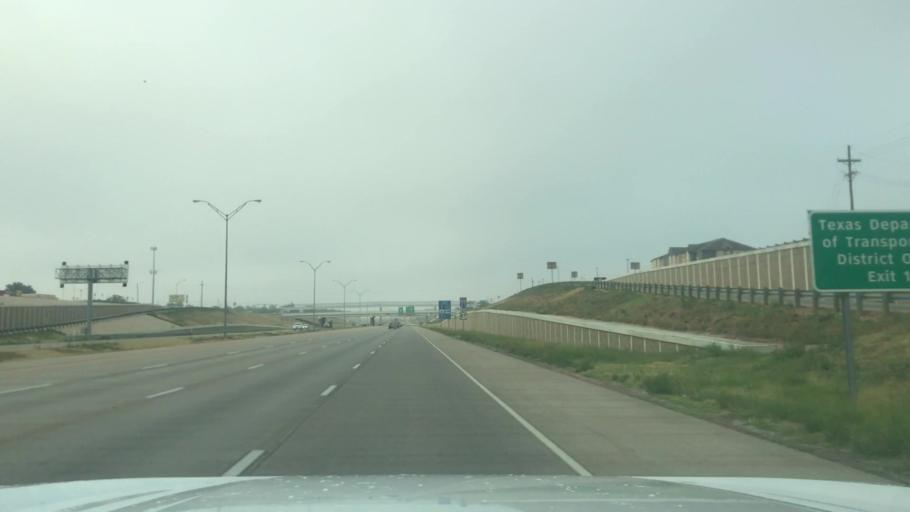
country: US
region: Texas
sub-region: Lubbock County
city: Lubbock
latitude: 33.5533
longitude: -101.8453
